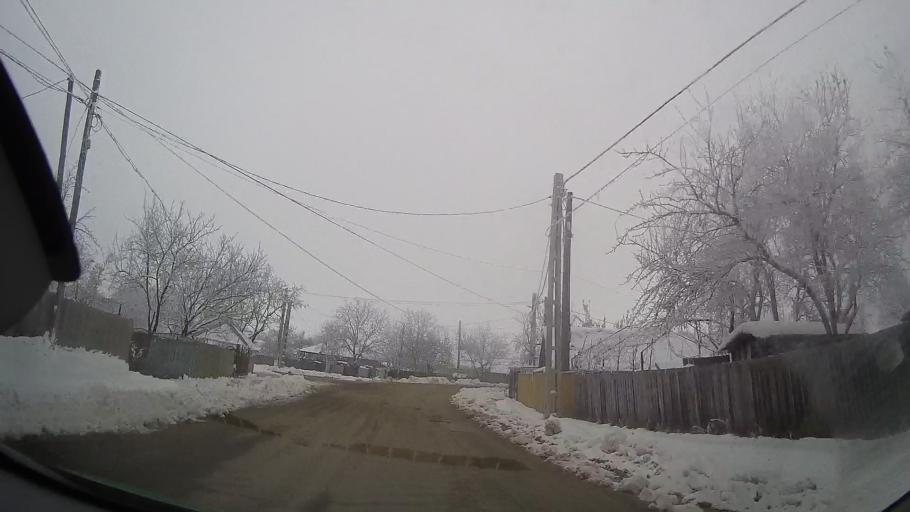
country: RO
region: Iasi
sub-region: Comuna Tansa
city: Tansa
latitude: 46.9097
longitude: 27.2272
